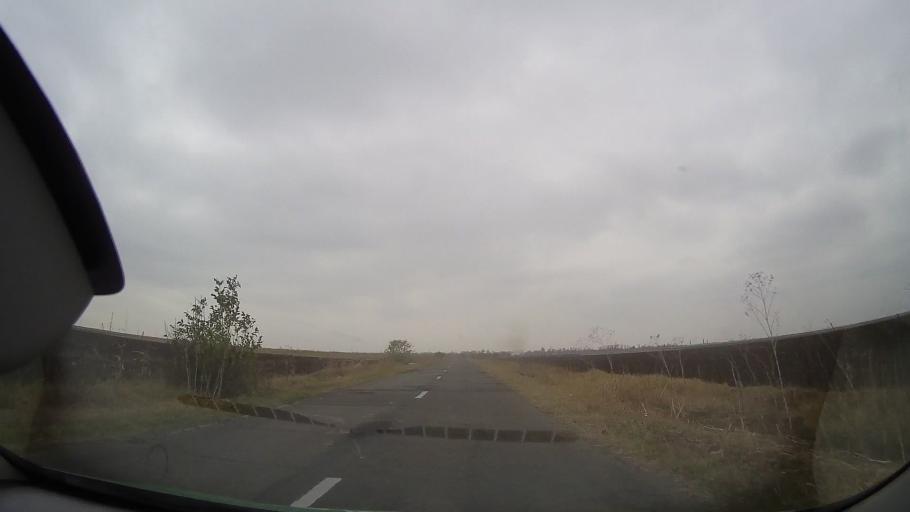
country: RO
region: Ialomita
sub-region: Comuna Valea Macrisului
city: Valea Macrisului
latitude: 44.7602
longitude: 26.8005
